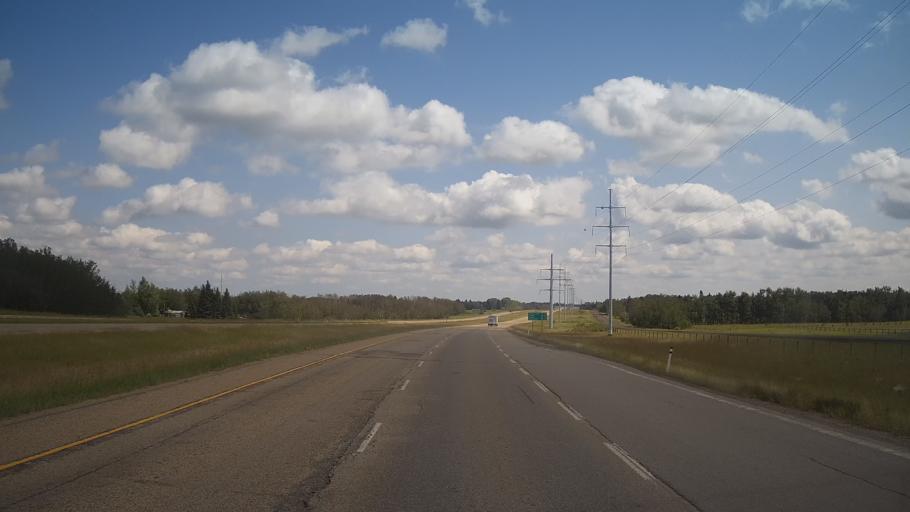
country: CA
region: Alberta
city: Sherwood Park
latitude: 53.4461
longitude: -113.2395
